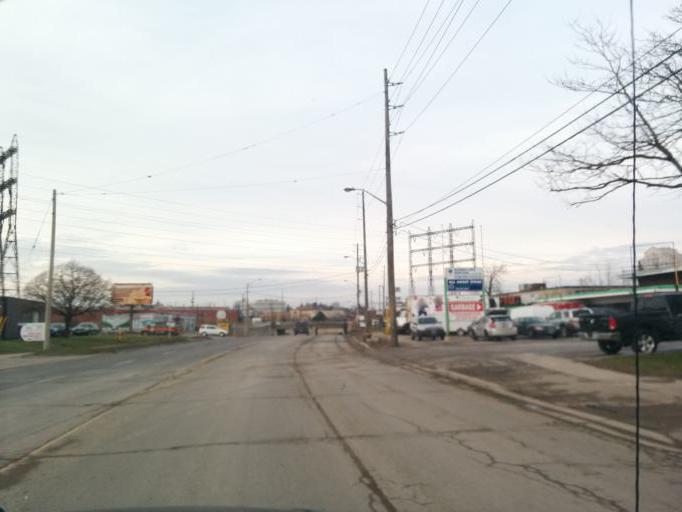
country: CA
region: Ontario
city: Etobicoke
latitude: 43.6284
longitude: -79.5432
